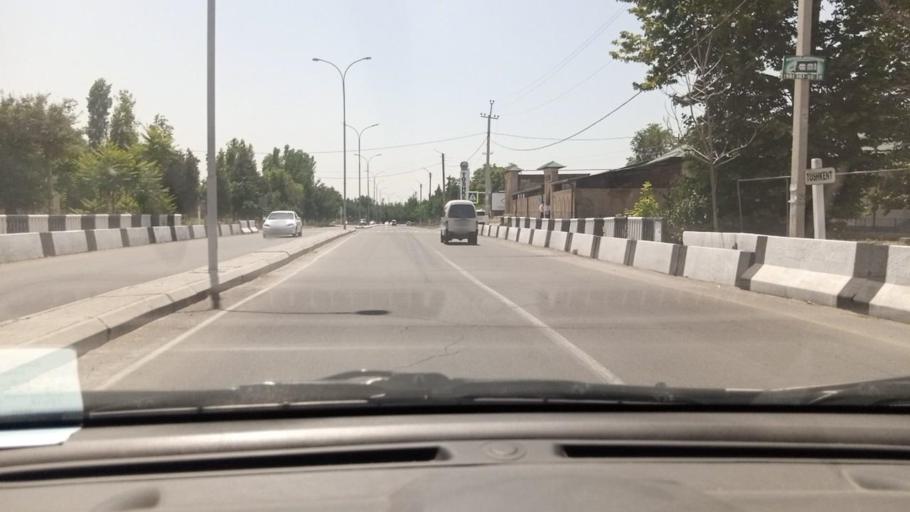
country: UZ
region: Toshkent
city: Urtaowul
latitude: 41.2199
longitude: 69.1750
